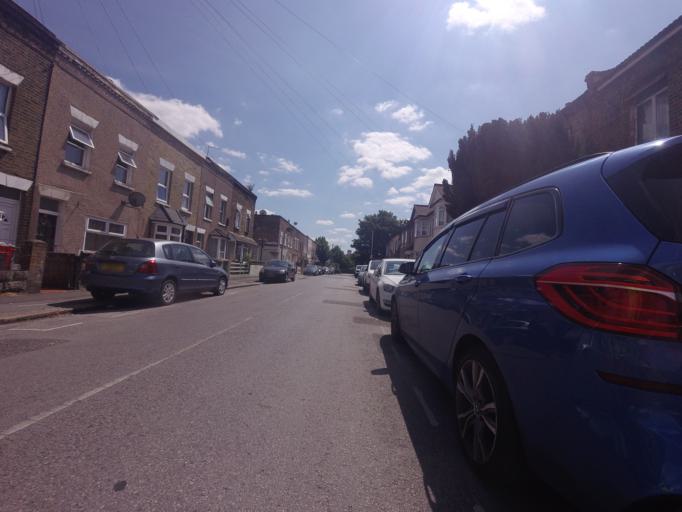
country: GB
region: England
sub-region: Greater London
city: East Ham
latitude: 51.5499
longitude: 0.0203
